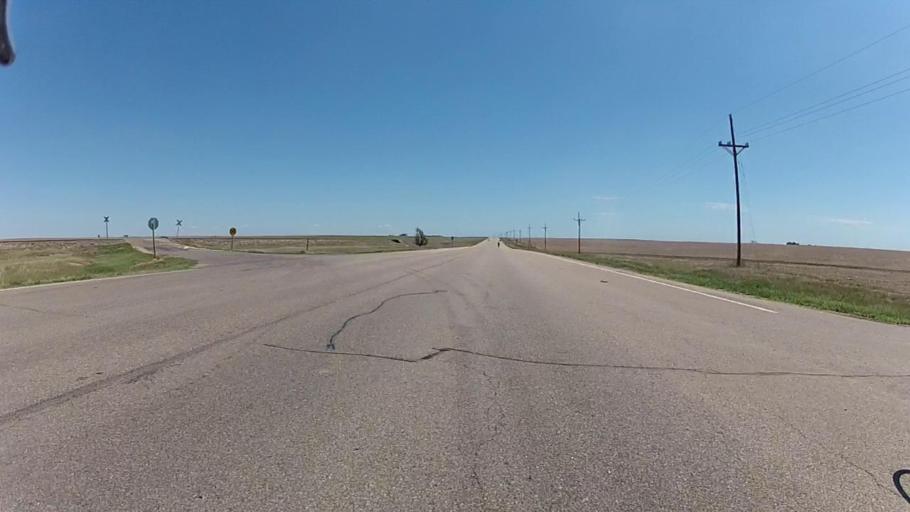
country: US
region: Kansas
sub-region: Ford County
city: Dodge City
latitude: 37.6838
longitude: -100.1790
